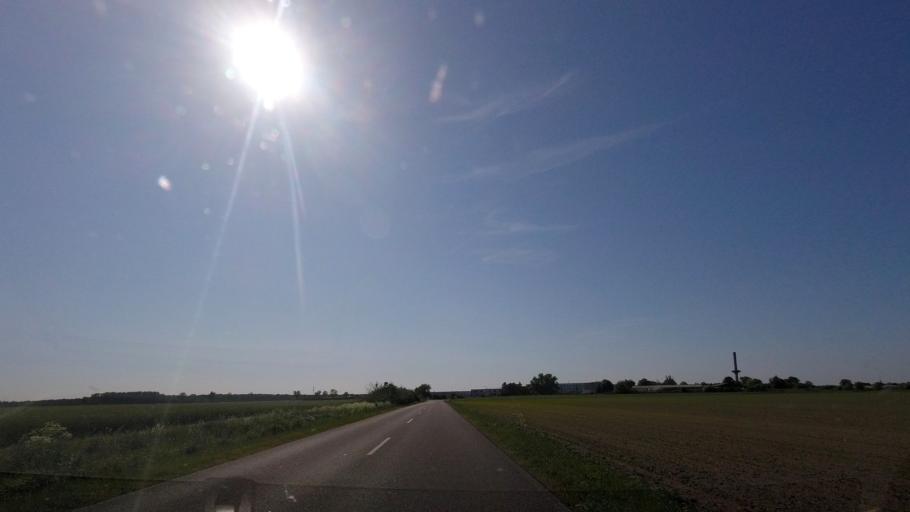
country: DE
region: Brandenburg
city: Brandenburg an der Havel
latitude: 52.3864
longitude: 12.6052
